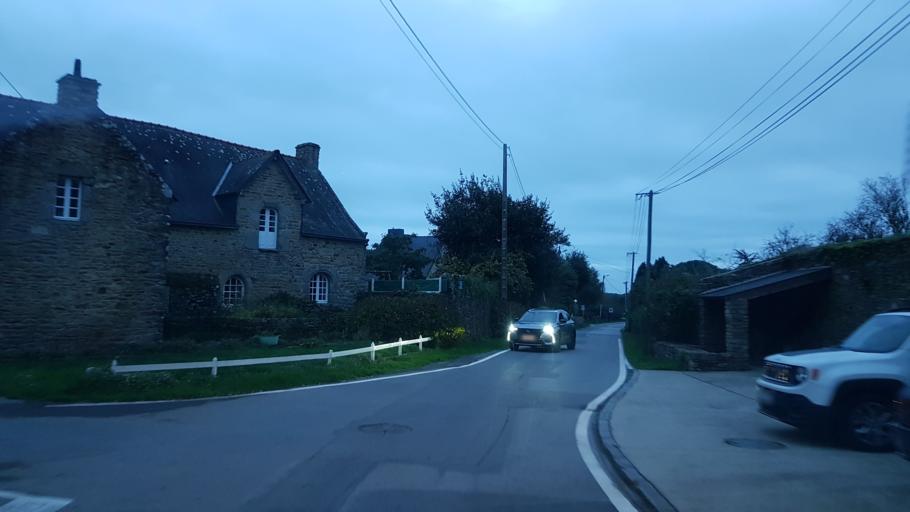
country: FR
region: Brittany
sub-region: Departement du Morbihan
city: Sarzeau
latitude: 47.5400
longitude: -2.7932
